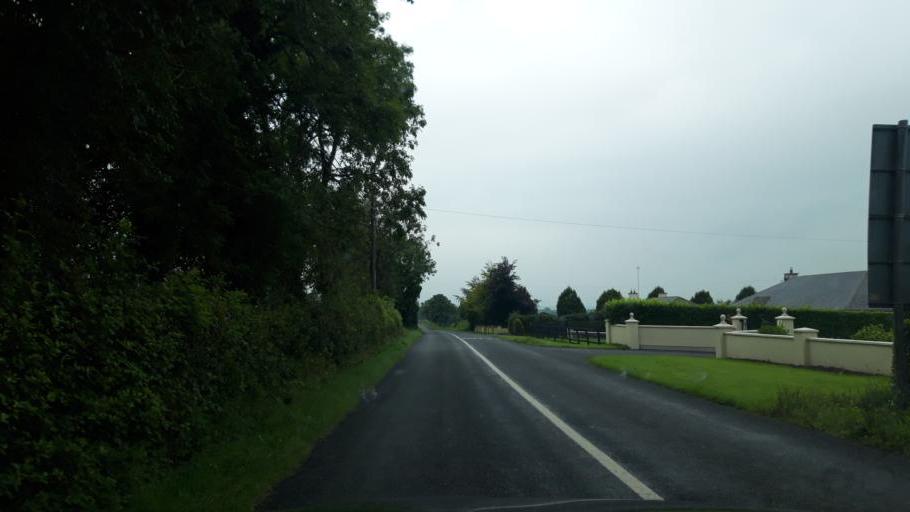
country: IE
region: Munster
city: Fethard
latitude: 52.5247
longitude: -7.6822
